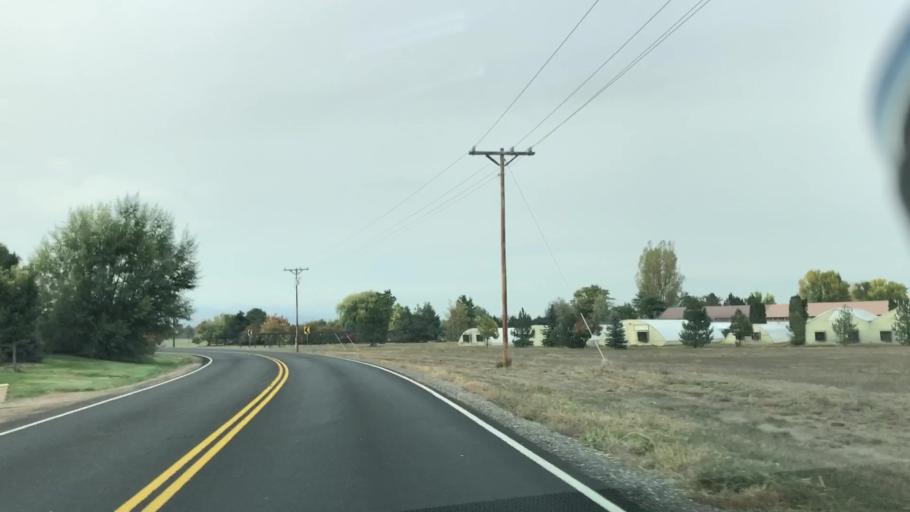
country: US
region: Colorado
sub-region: Larimer County
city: Loveland
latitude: 40.4672
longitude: -105.0546
